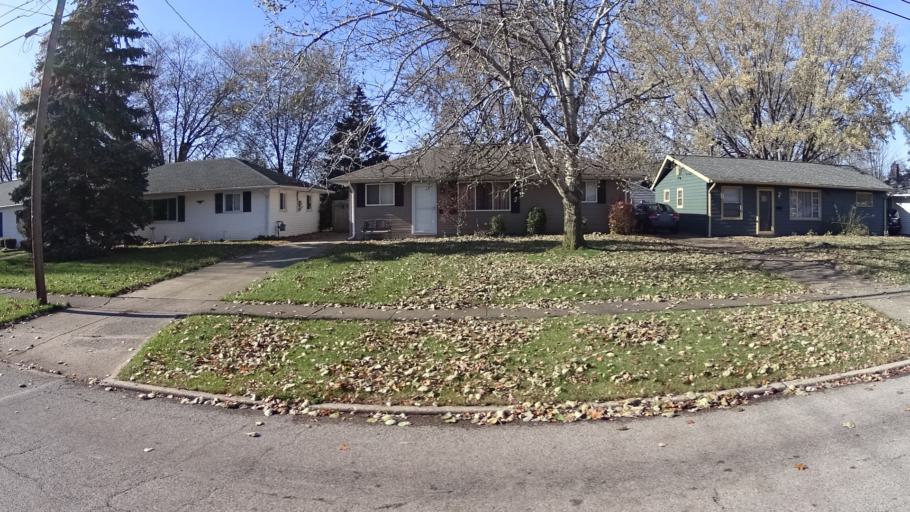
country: US
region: Ohio
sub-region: Lorain County
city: Sheffield Lake
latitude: 41.4961
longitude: -82.0699
